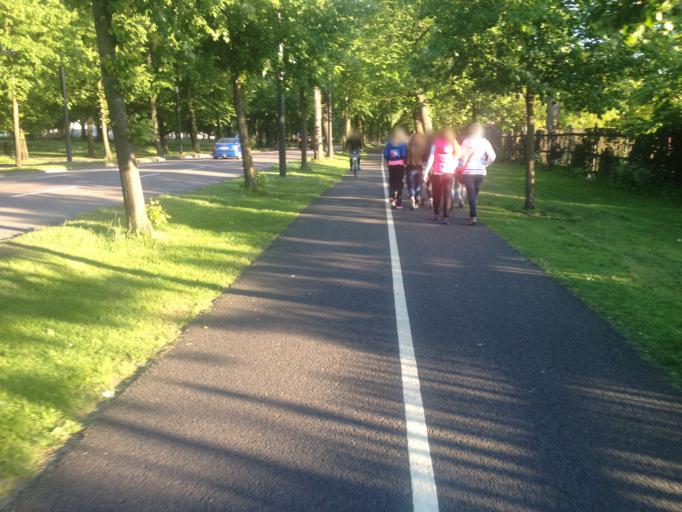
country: SE
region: Vaestra Goetaland
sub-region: Goteborg
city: Goeteborg
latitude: 57.7068
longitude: 11.9776
